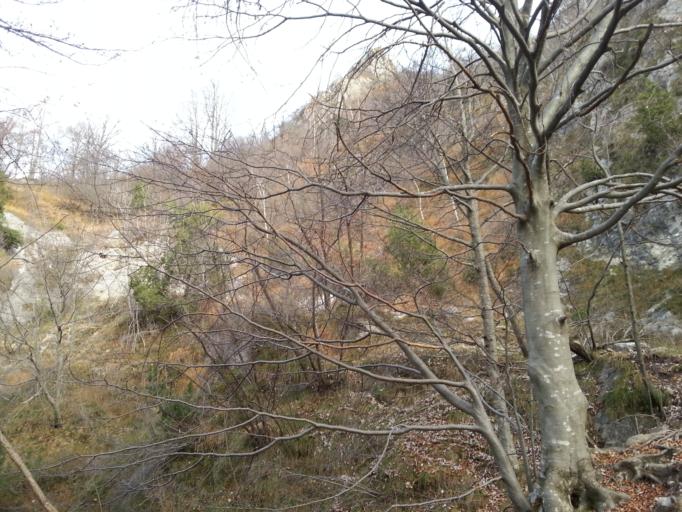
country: IT
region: Lombardy
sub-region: Provincia di Lecco
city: Morterone
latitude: 45.8910
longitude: 9.4670
